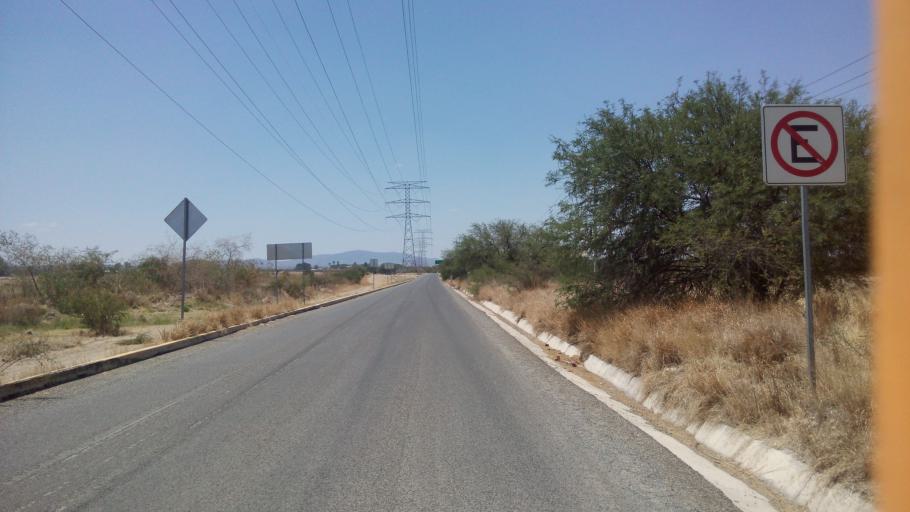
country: MX
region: Aguascalientes
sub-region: Aguascalientes
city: San Sebastian [Fraccionamiento]
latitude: 21.7975
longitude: -102.2886
